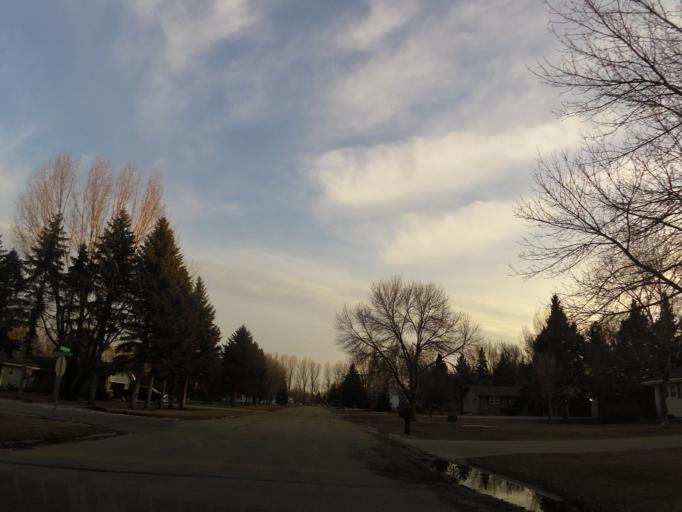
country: US
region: North Dakota
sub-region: Grand Forks County
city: Grand Forks
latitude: 47.8556
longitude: -97.0116
